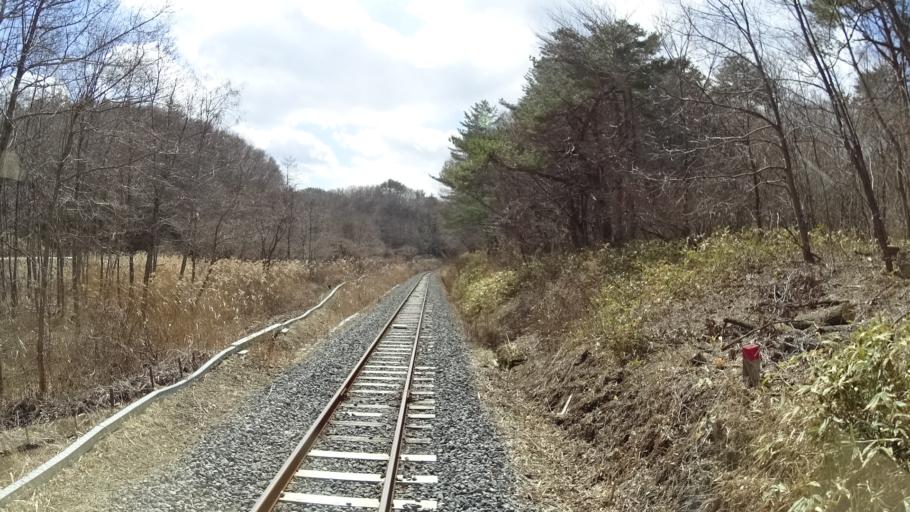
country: JP
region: Iwate
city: Yamada
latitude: 39.4958
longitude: 141.9284
